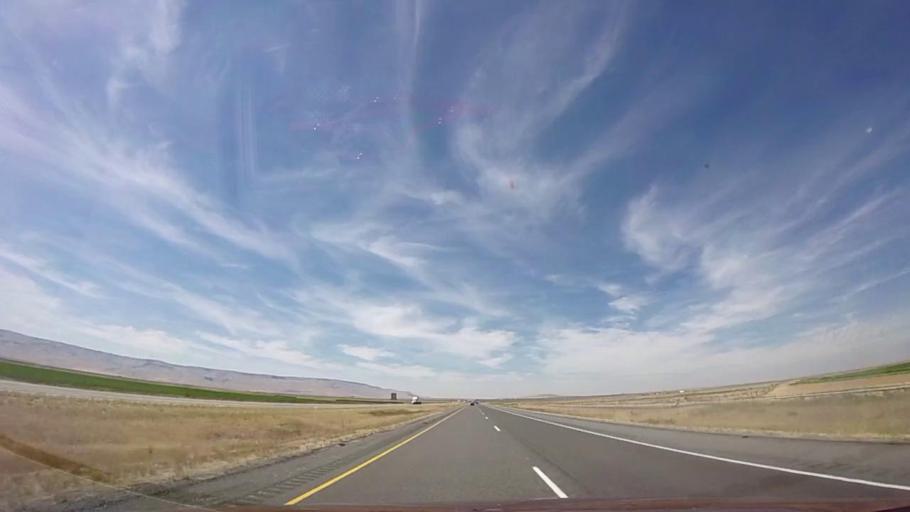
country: US
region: Idaho
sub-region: Minidoka County
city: Rupert
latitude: 42.4272
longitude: -113.3329
